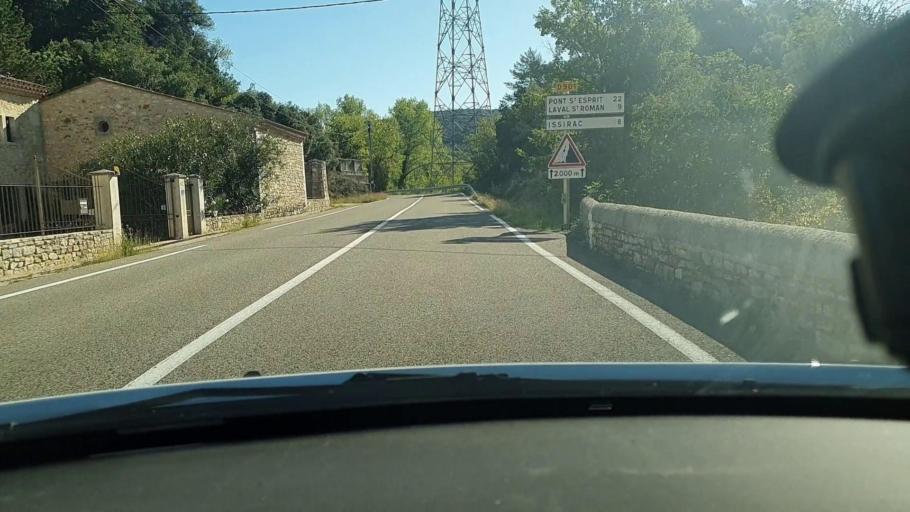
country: FR
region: Languedoc-Roussillon
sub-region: Departement du Gard
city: Goudargues
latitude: 44.2700
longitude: 4.4270
